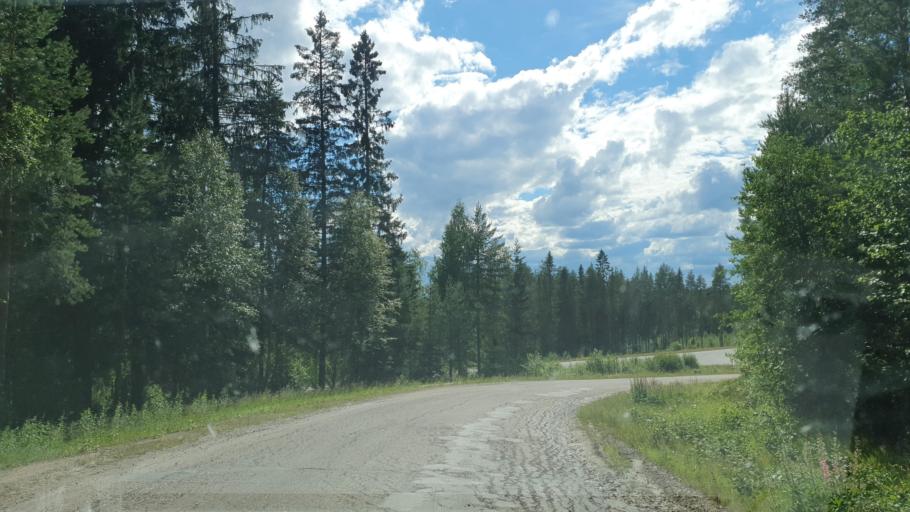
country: FI
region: Kainuu
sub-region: Kehys-Kainuu
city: Kuhmo
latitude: 64.1259
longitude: 29.6415
